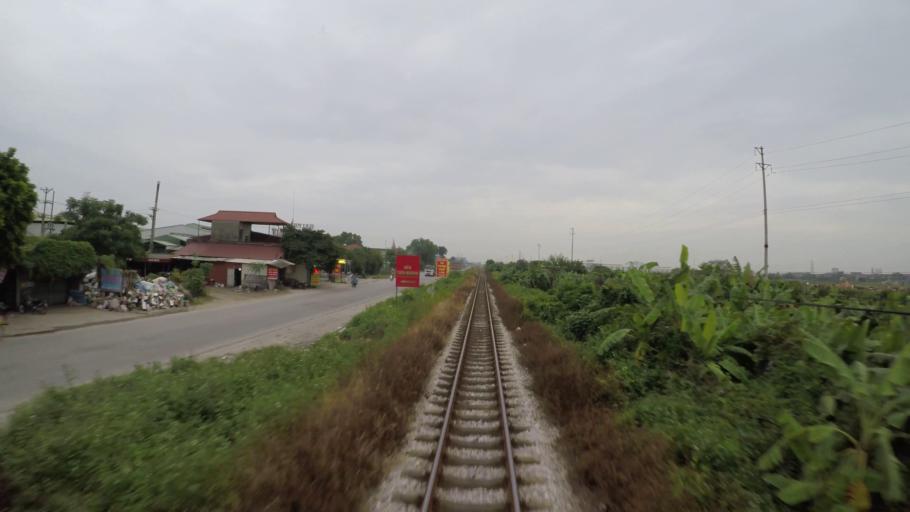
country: VN
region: Hung Yen
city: Nhu Quynh
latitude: 20.9835
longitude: 106.0321
